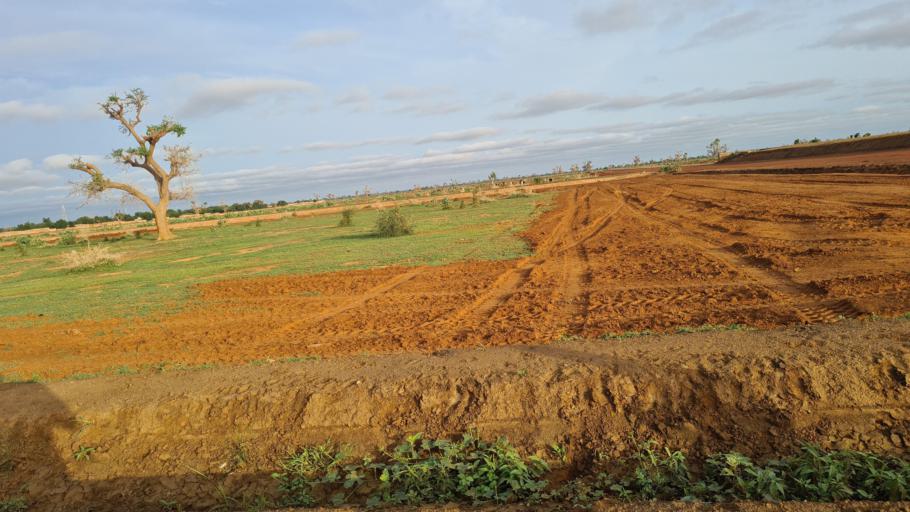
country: NE
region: Tahoua
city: Birni N Konni
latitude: 13.7879
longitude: 5.2338
